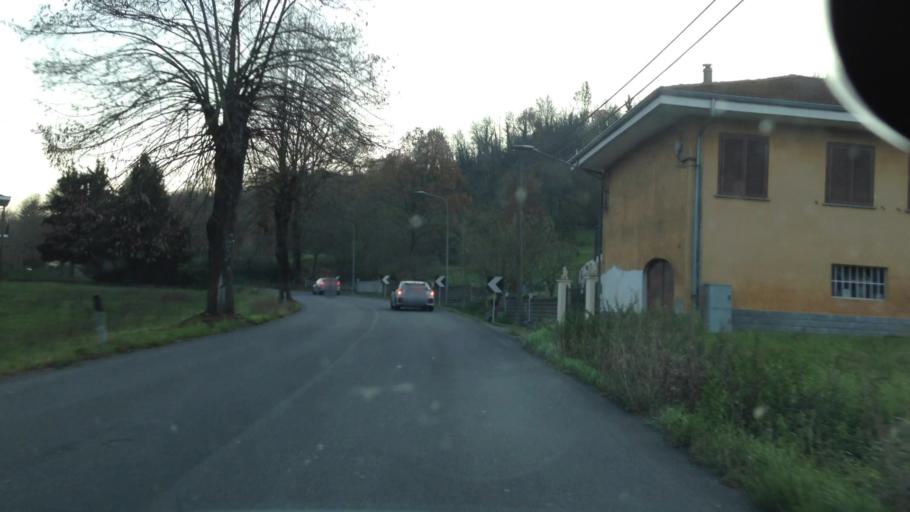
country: IT
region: Piedmont
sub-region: Provincia di Torino
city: Cavagnolo
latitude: 45.1360
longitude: 8.0551
